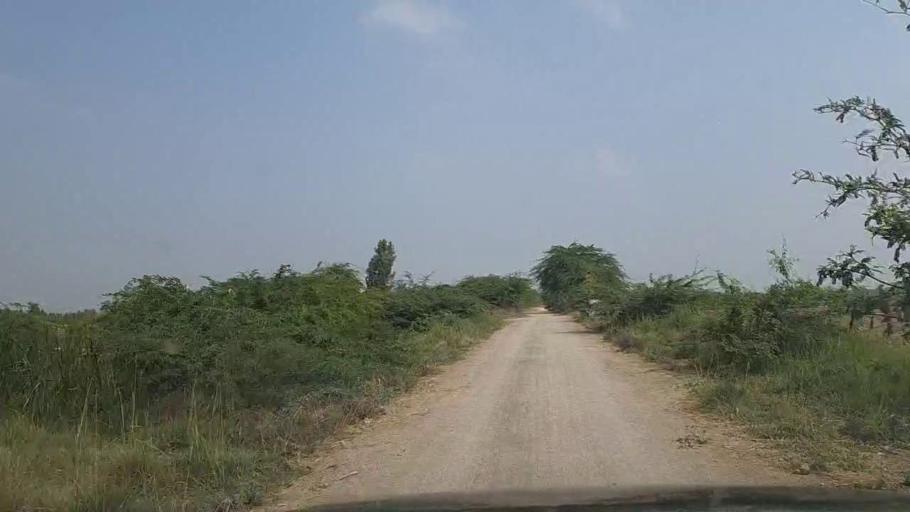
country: PK
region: Sindh
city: Thatta
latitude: 24.7752
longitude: 67.8306
